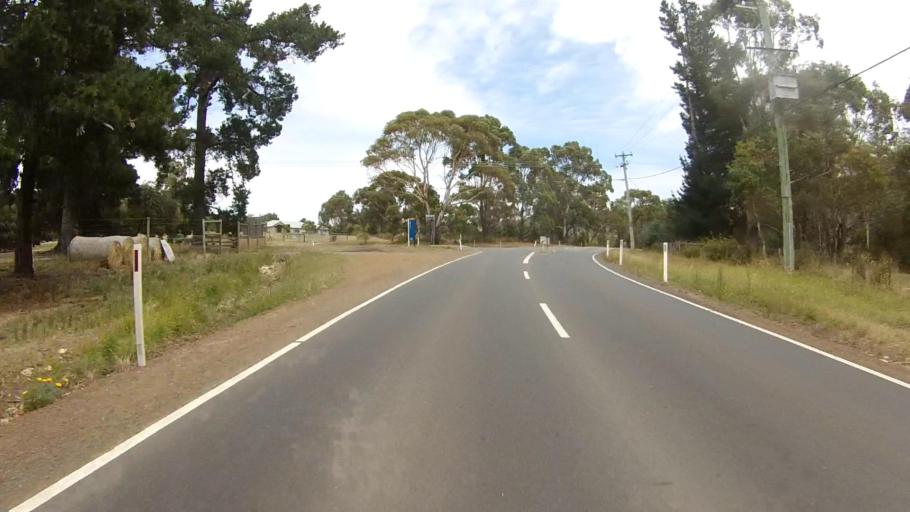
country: AU
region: Tasmania
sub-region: Clarence
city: Acton Park
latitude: -42.8674
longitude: 147.4873
